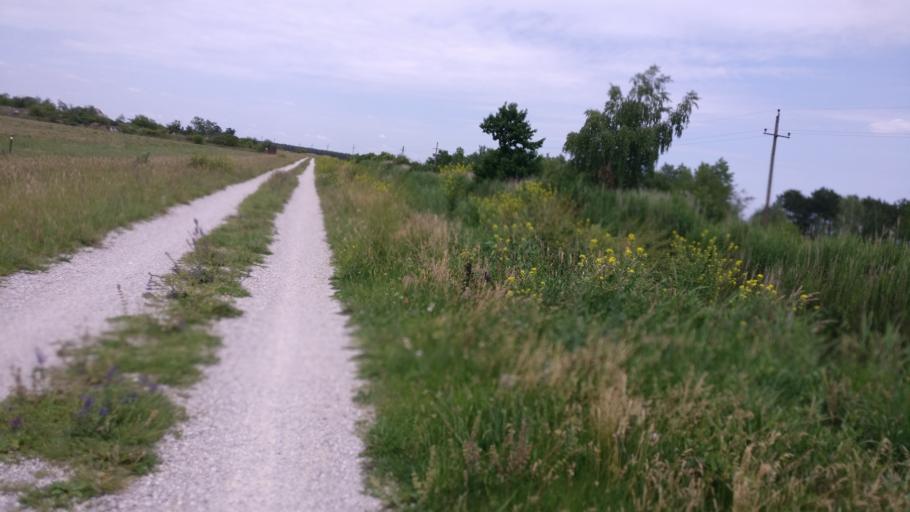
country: AT
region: Lower Austria
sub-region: Politischer Bezirk Wiener Neustadt
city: Lichtenworth
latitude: 47.8495
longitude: 16.2775
